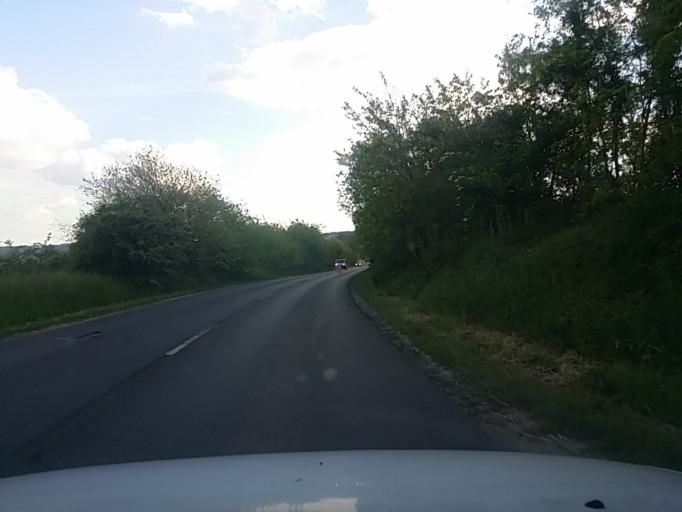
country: HU
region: Pest
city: Mogyorod
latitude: 47.6498
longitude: 19.2360
